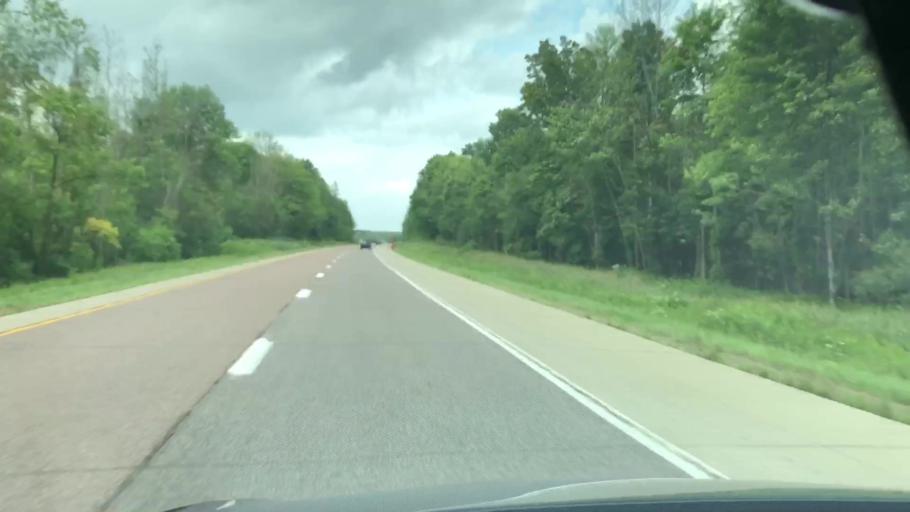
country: US
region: Pennsylvania
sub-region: Erie County
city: Edinboro
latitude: 41.9465
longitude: -80.1736
